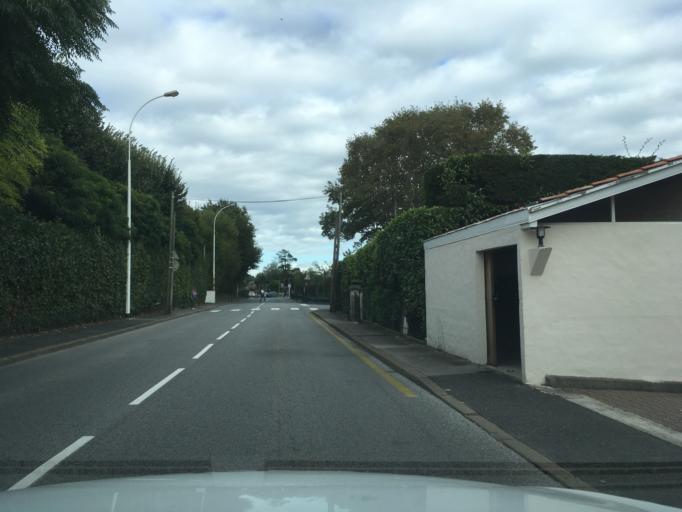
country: FR
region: Aquitaine
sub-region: Departement des Pyrenees-Atlantiques
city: Biarritz
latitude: 43.4621
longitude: -1.5551
